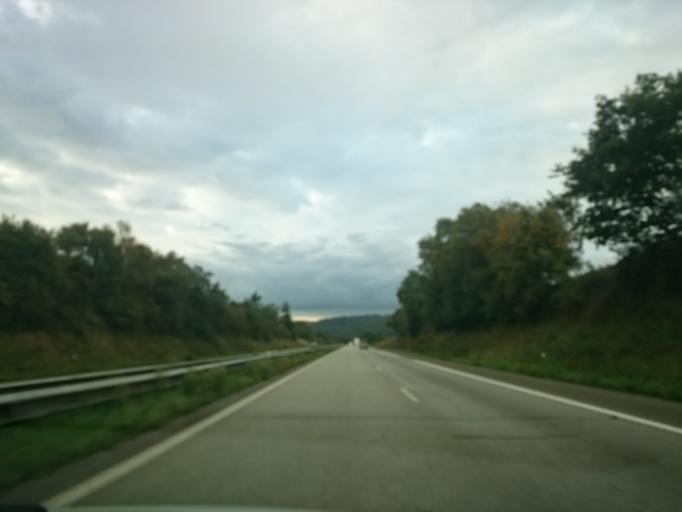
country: FR
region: Brittany
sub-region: Departement du Finistere
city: Chateaulin
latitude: 48.1965
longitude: -4.0445
